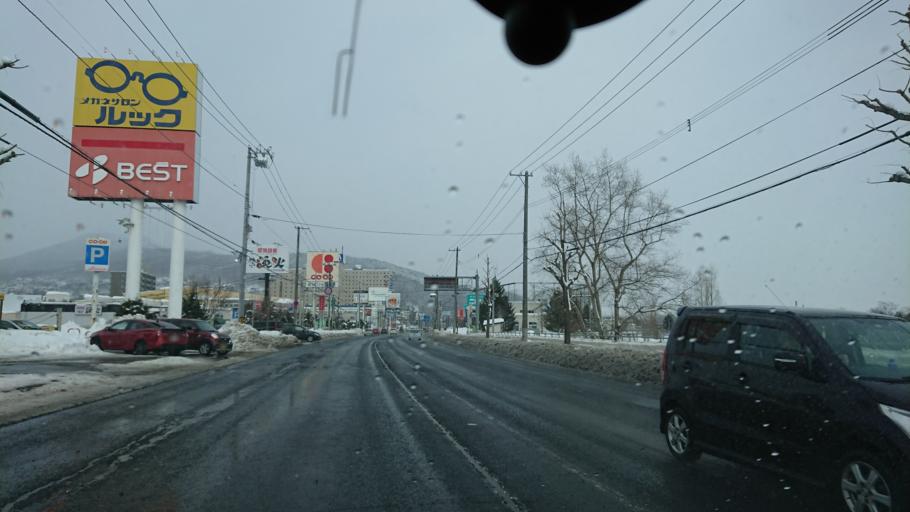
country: JP
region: Hokkaido
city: Sapporo
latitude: 42.9902
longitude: 141.3344
